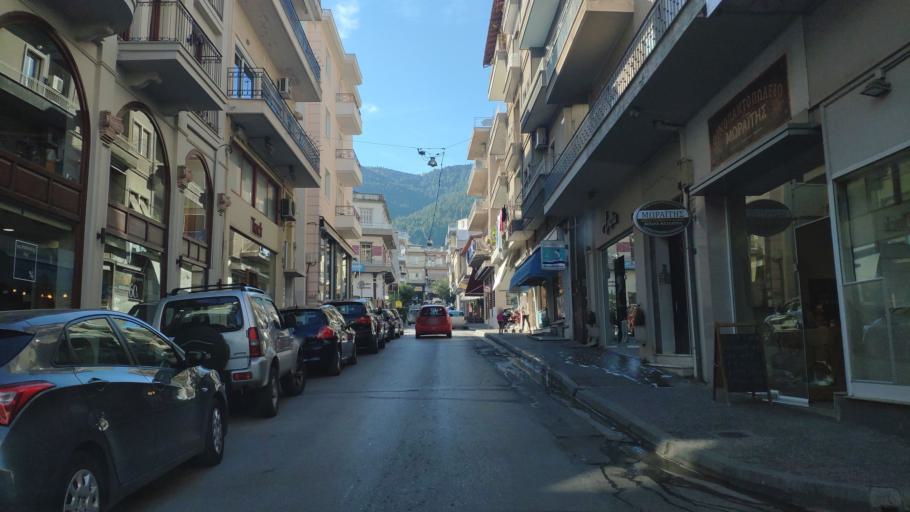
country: GR
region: Central Greece
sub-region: Nomos Voiotias
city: Livadeia
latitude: 38.4384
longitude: 22.8778
